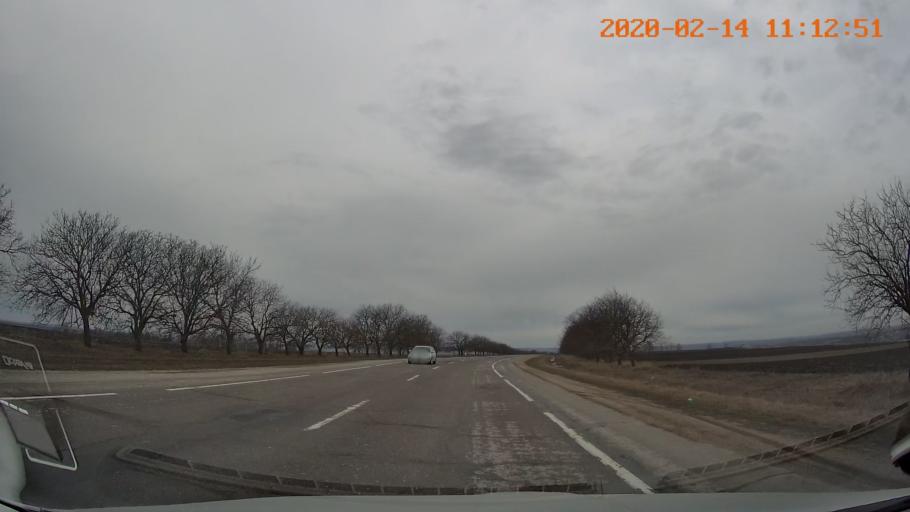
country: MD
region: Raionul Edinet
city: Edinet
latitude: 48.2094
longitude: 27.2525
